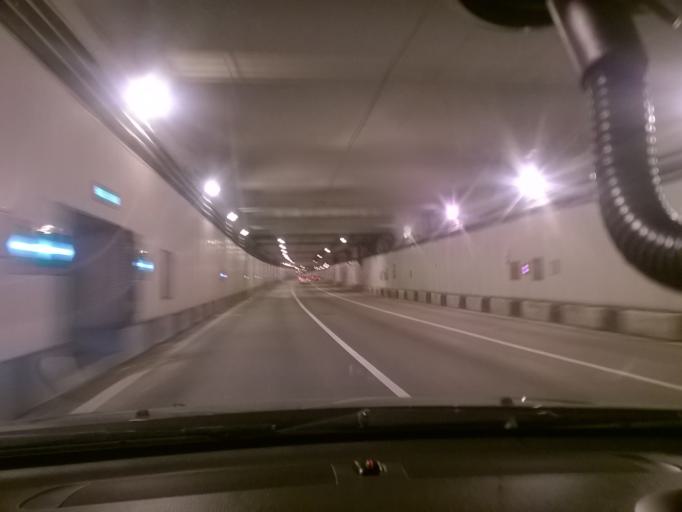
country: RU
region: Moskovskaya
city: Koptevo
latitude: 55.8144
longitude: 37.5180
